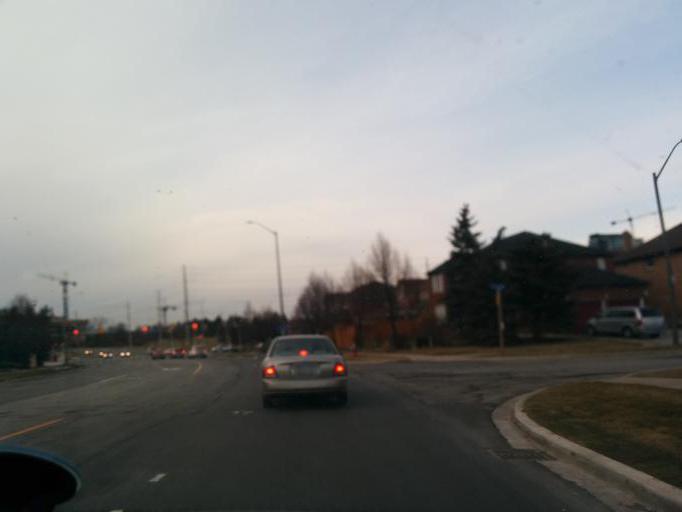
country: CA
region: Ontario
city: Mississauga
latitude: 43.5517
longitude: -79.7065
